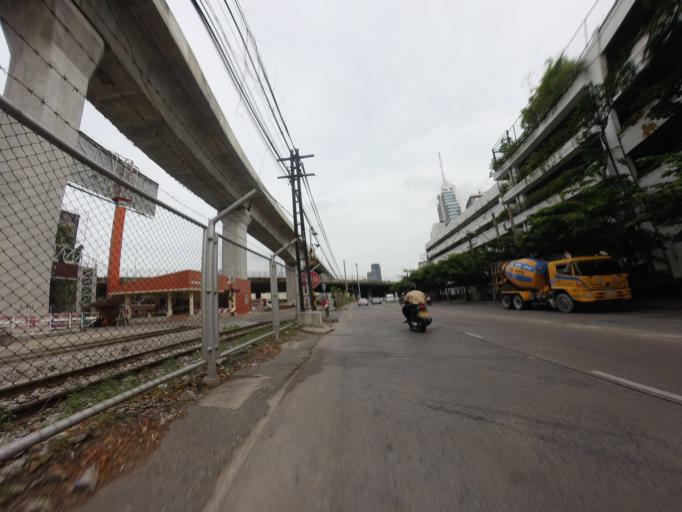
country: TH
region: Bangkok
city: Ratchathewi
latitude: 13.7543
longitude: 100.5450
